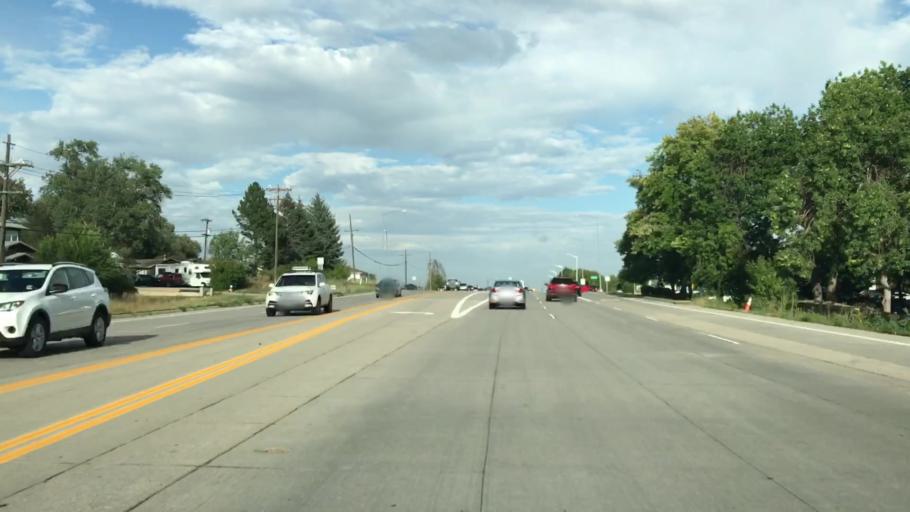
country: US
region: Colorado
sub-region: Boulder County
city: Longmont
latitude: 40.2032
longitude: -105.1085
